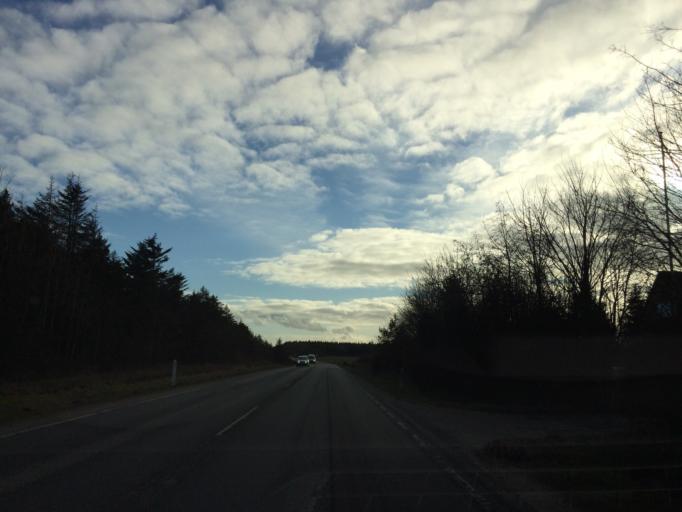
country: DK
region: Central Jutland
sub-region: Lemvig Kommune
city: Lemvig
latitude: 56.4844
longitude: 8.2984
